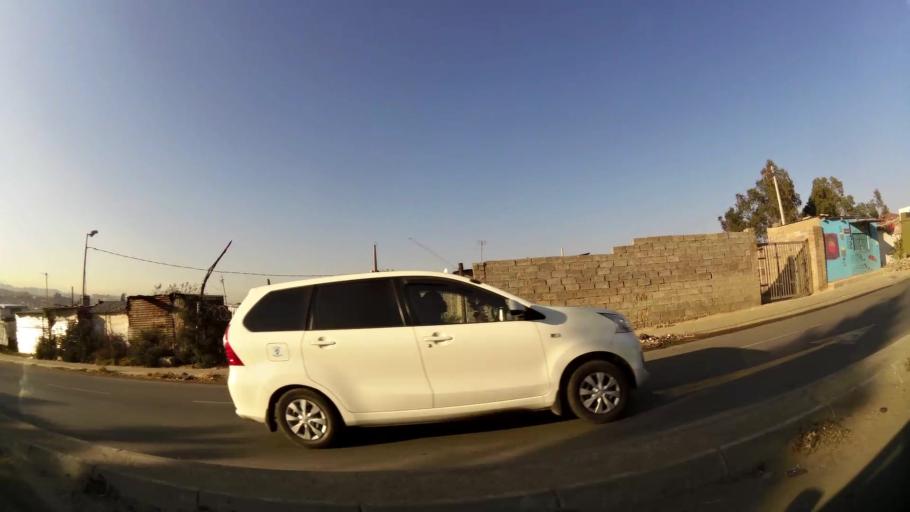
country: ZA
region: Gauteng
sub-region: City of Johannesburg Metropolitan Municipality
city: Modderfontein
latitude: -26.0963
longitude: 28.1022
